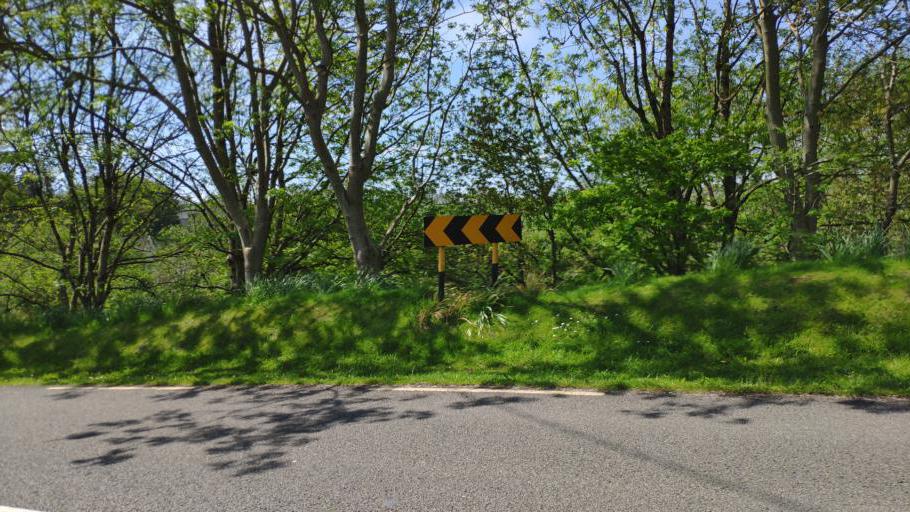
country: IE
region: Munster
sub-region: County Cork
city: Blarney
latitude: 51.9550
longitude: -8.5755
